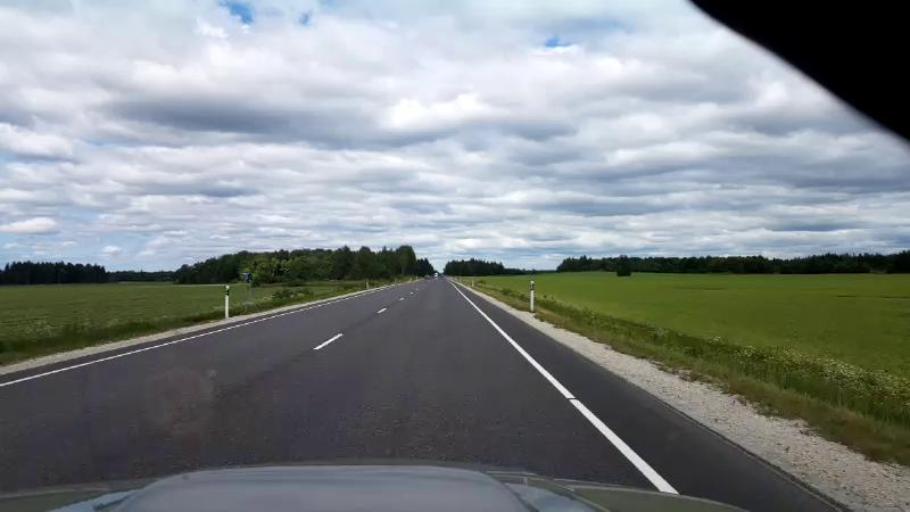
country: EE
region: Raplamaa
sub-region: Maerjamaa vald
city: Marjamaa
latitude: 58.8492
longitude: 24.4294
